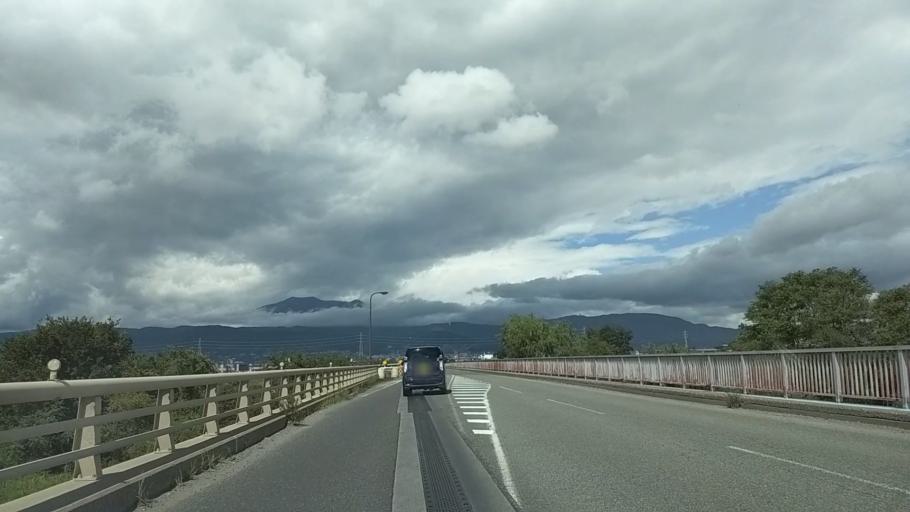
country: JP
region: Nagano
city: Nagano-shi
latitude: 36.6216
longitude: 138.2400
